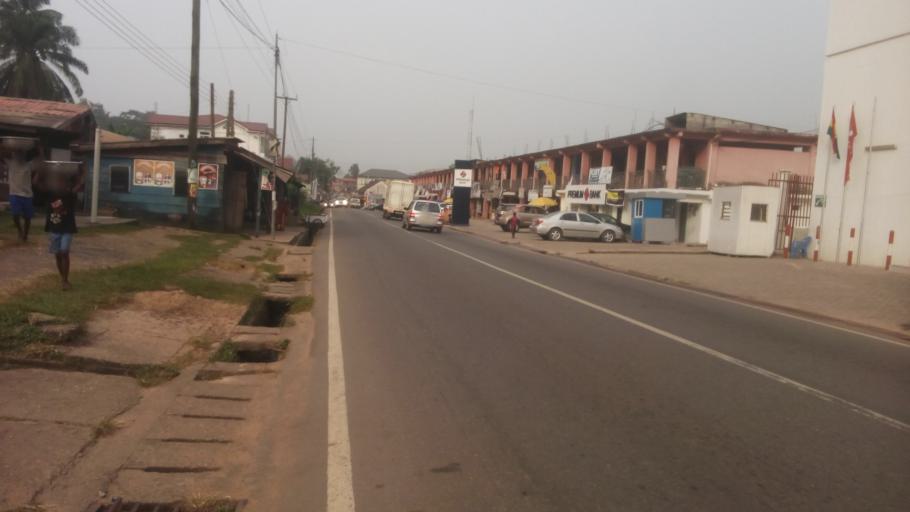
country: GH
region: Western
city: Tarkwa
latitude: 5.3021
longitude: -1.9929
